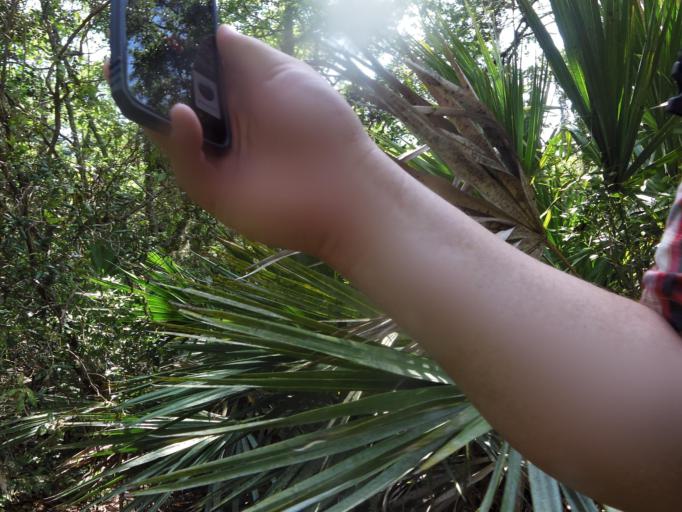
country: US
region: Florida
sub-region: Nassau County
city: Yulee
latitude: 30.4940
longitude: -81.5008
